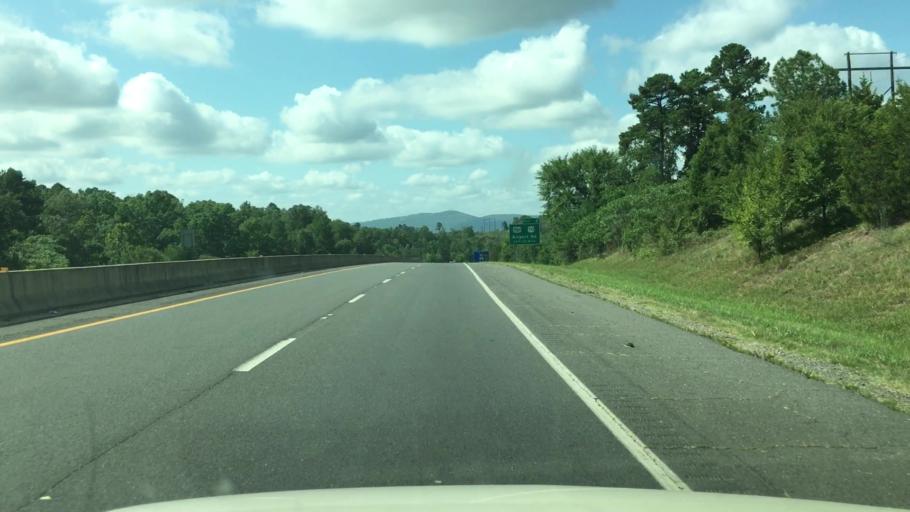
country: US
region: Arkansas
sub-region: Garland County
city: Piney
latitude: 34.4887
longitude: -93.1119
